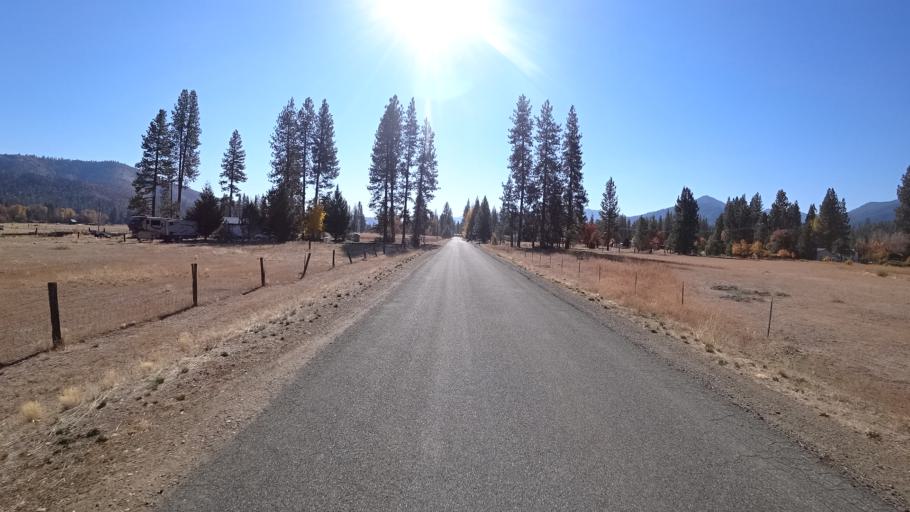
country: US
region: California
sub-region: Siskiyou County
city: Yreka
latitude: 41.6078
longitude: -122.9699
